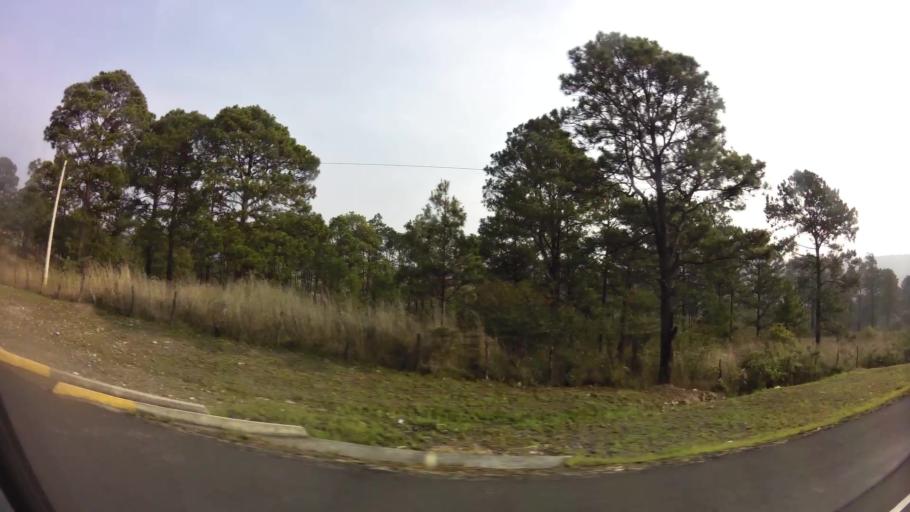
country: HN
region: Francisco Morazan
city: Zambrano
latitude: 14.2515
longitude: -87.3796
